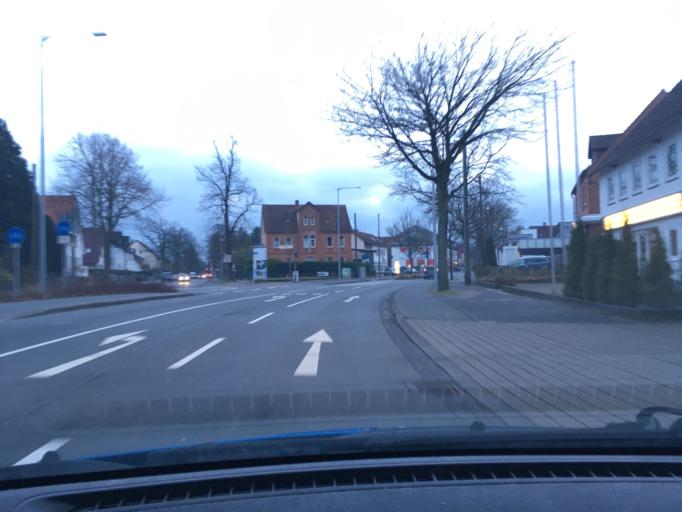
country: DE
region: Lower Saxony
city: Celle
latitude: 52.6140
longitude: 10.0793
